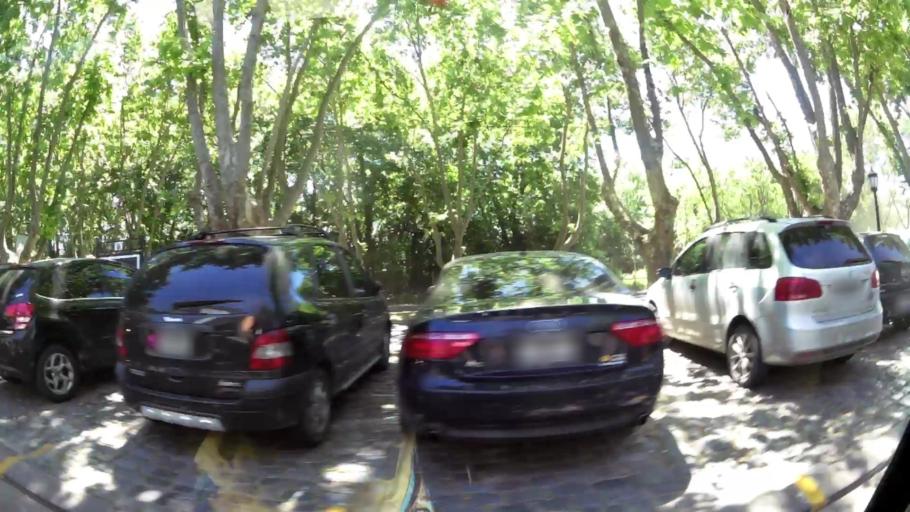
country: AR
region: Buenos Aires
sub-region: Partido de San Isidro
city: San Isidro
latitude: -34.4903
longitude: -58.5256
